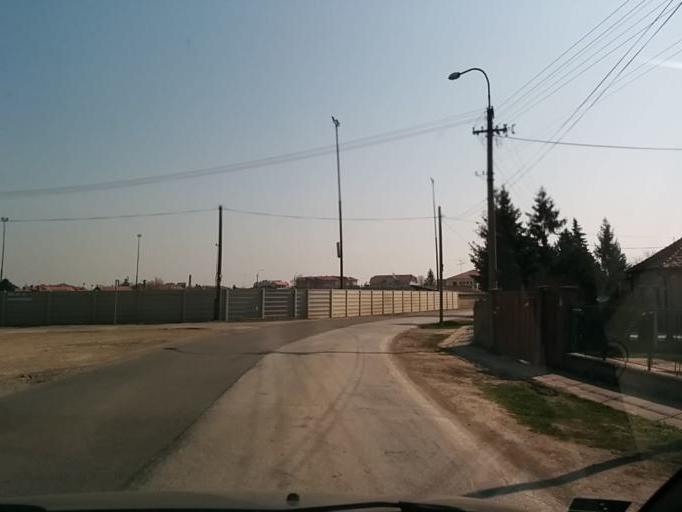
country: SK
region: Trnavsky
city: Sladkovicovo
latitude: 48.2050
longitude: 17.6339
